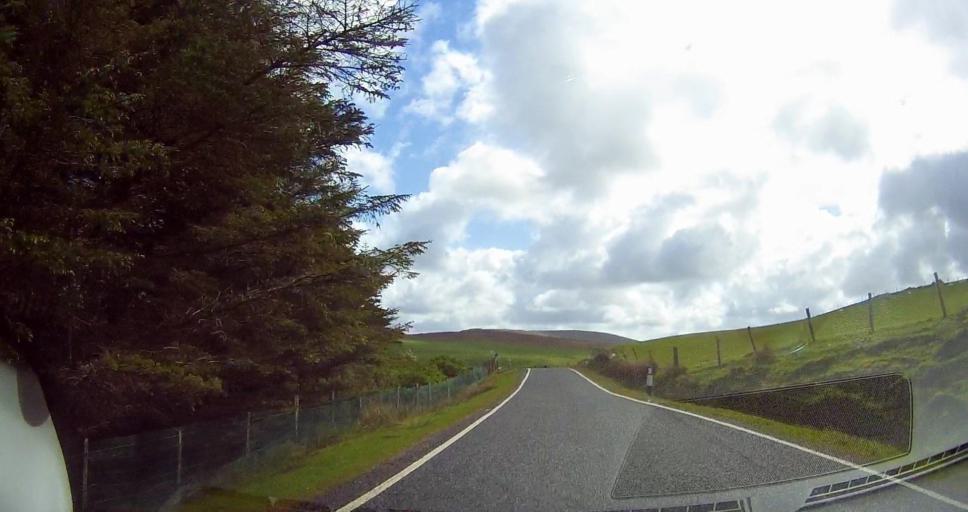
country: GB
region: Scotland
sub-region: Shetland Islands
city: Lerwick
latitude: 60.5318
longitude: -1.3624
